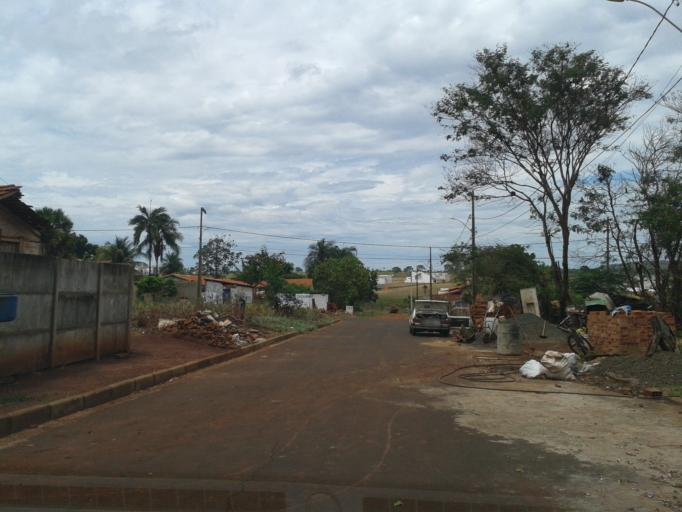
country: BR
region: Minas Gerais
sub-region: Ituiutaba
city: Ituiutaba
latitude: -18.9965
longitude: -49.4621
